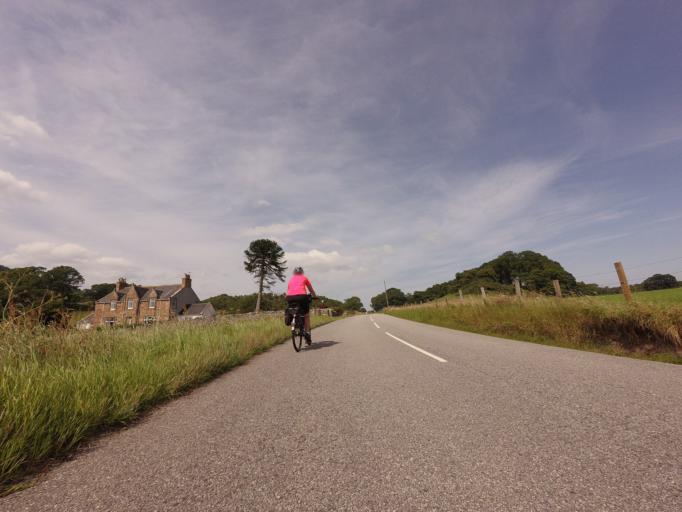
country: GB
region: Scotland
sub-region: Highland
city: Tain
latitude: 57.8492
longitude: -4.2030
